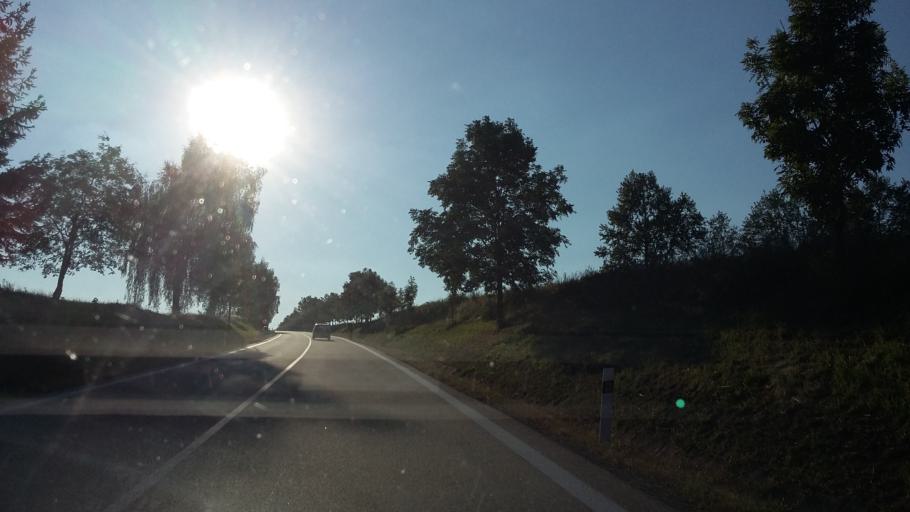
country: CZ
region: Vysocina
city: Merin
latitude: 49.4003
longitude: 15.8516
